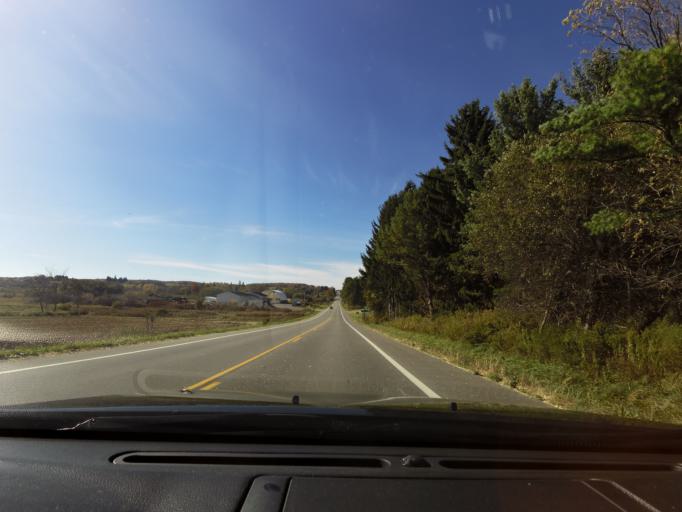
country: US
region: New York
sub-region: Wyoming County
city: Warsaw
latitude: 42.6502
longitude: -78.1893
